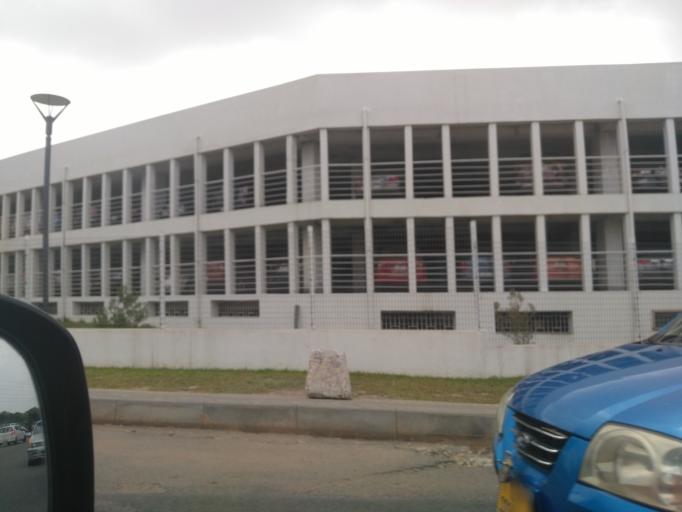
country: GH
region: Greater Accra
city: Accra
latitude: 5.5998
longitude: -0.1796
